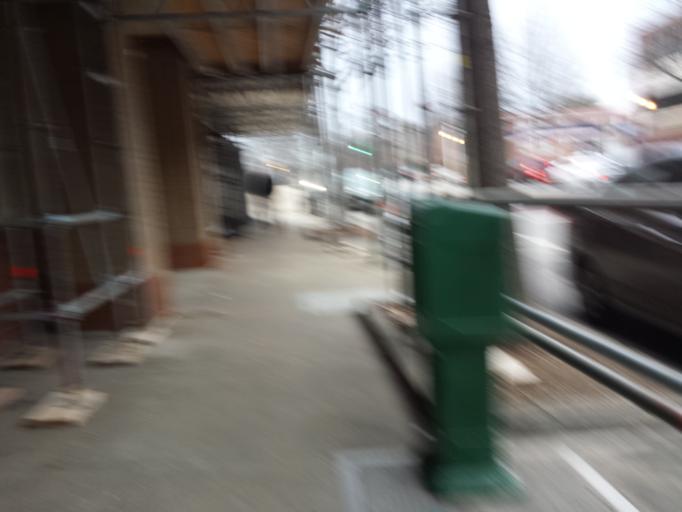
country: US
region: Georgia
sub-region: DeKalb County
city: Decatur
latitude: 33.7755
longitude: -84.2939
